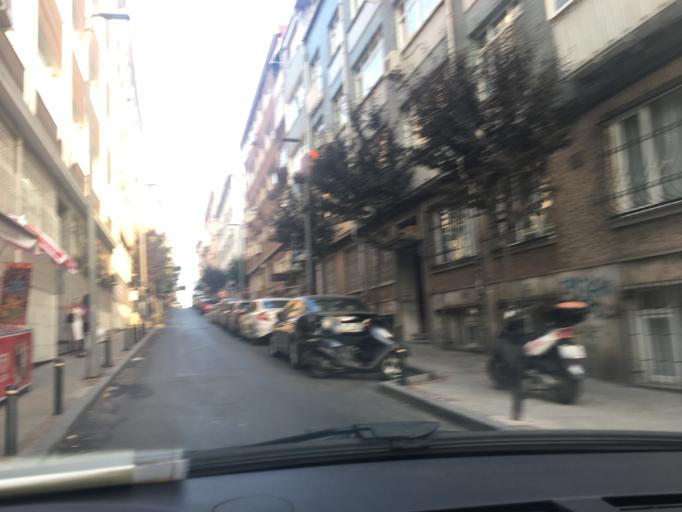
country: TR
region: Istanbul
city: Sisli
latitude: 41.0505
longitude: 28.9802
